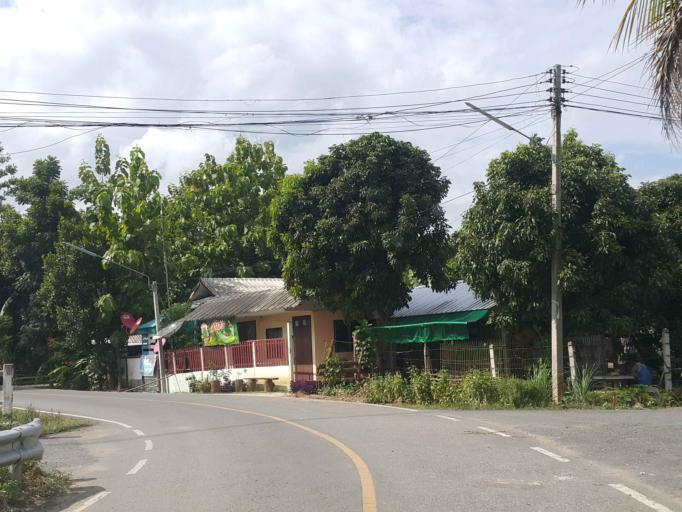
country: TH
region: Chiang Mai
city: Saraphi
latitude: 18.7327
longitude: 99.0602
